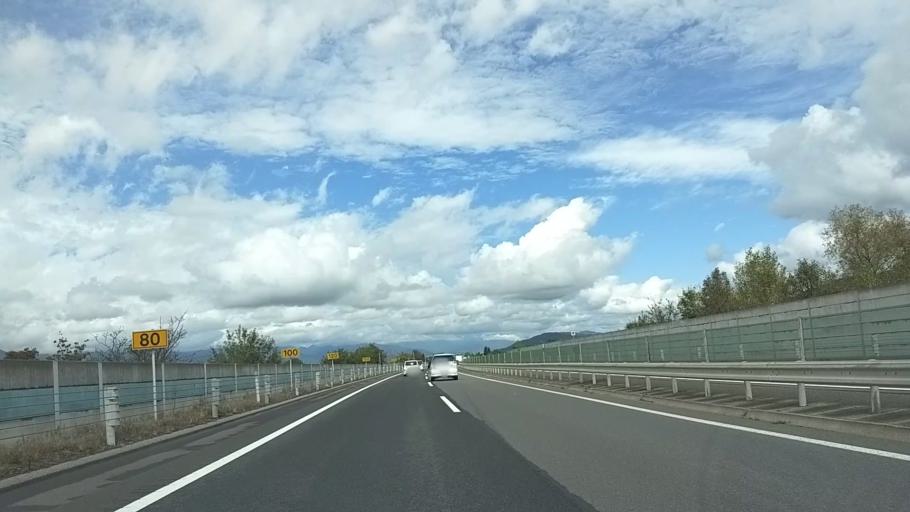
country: JP
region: Nagano
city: Toyoshina
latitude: 36.2852
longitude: 137.9293
